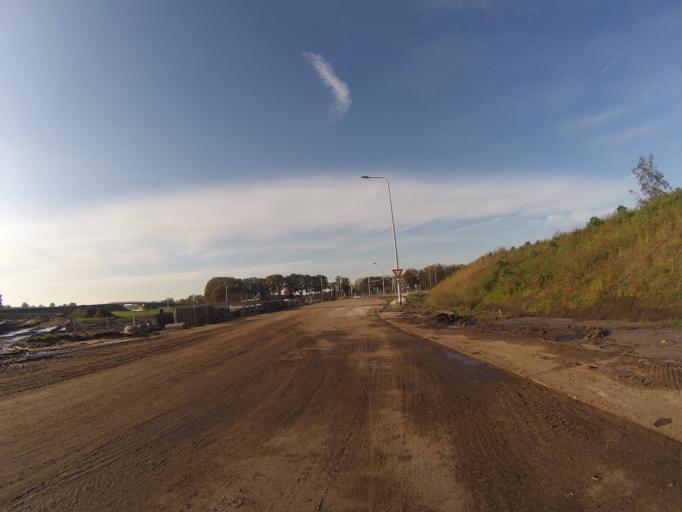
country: NL
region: Gelderland
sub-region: Gemeente Barneveld
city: Voorthuizen
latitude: 52.1933
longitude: 5.6042
